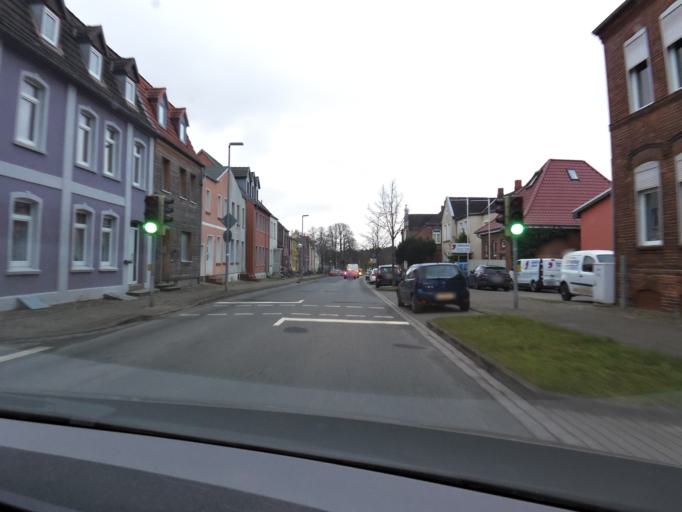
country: DE
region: Mecklenburg-Vorpommern
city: Grevesmuhlen
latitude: 53.8599
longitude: 11.1811
